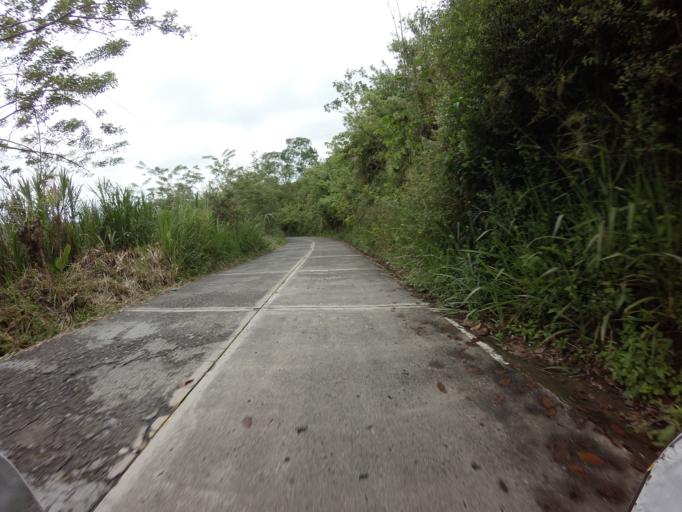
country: CO
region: Valle del Cauca
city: Alcala
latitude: 4.6979
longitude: -75.7701
